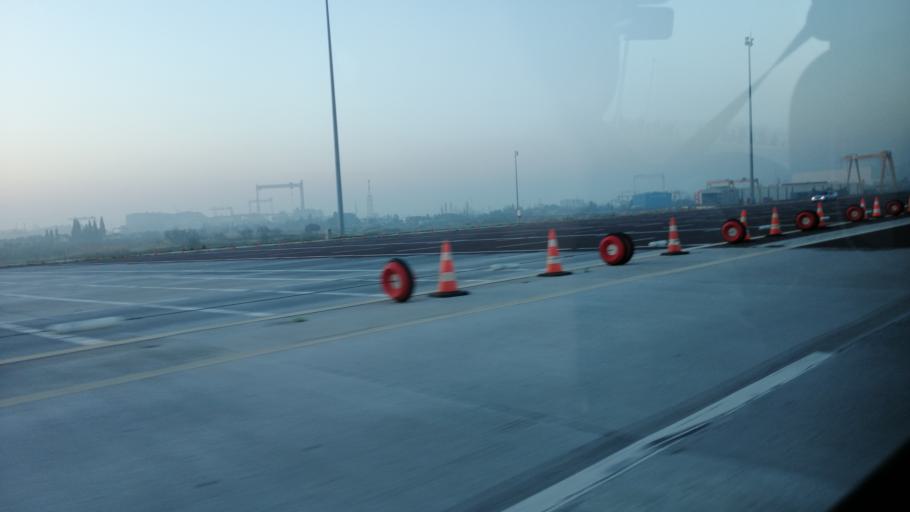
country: TR
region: Yalova
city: Altinova
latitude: 40.7169
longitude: 29.5008
